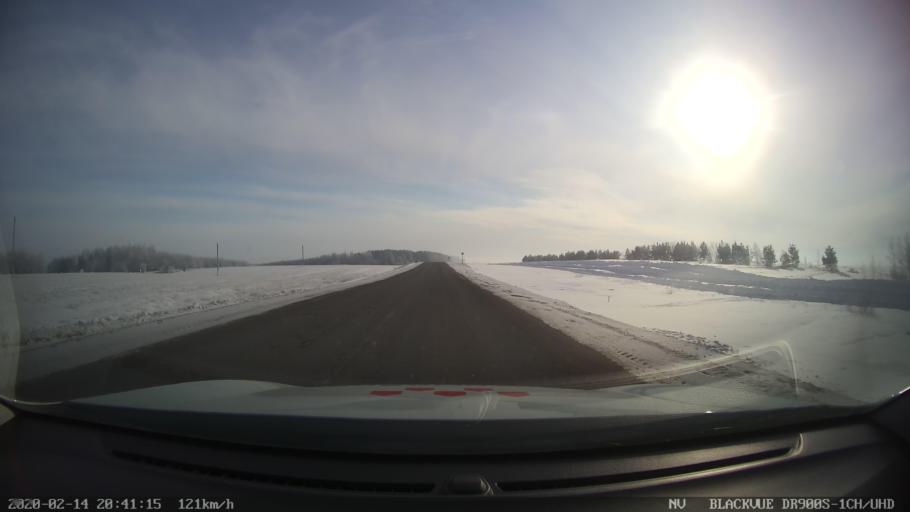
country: RU
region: Tatarstan
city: Kuybyshevskiy Zaton
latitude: 55.3324
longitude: 49.1145
